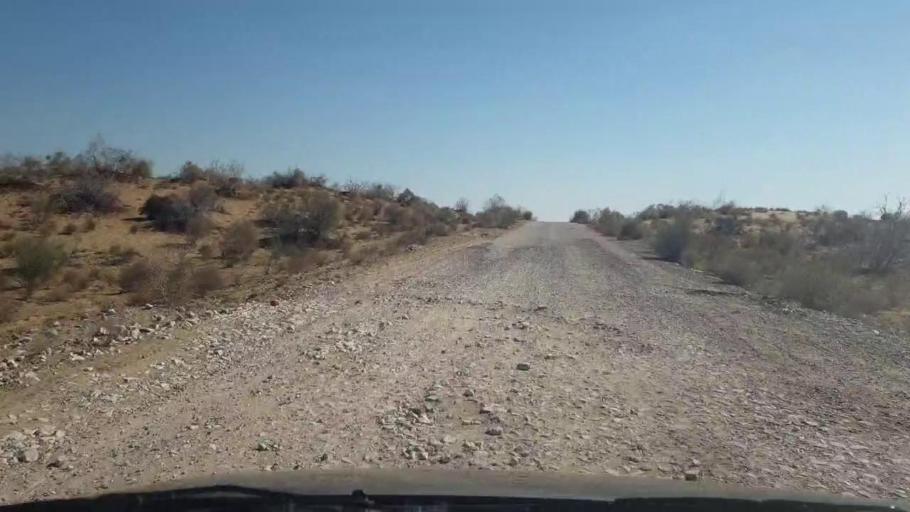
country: PK
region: Sindh
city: Bozdar
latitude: 27.0267
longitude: 68.7101
